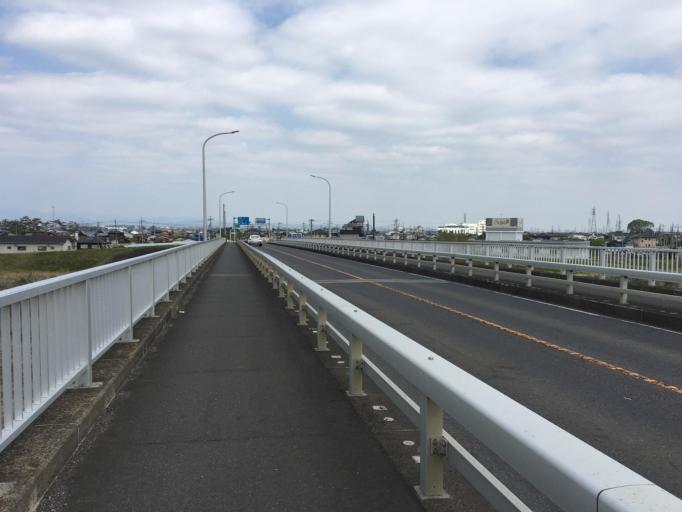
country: JP
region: Gunma
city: Isesaki
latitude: 36.2900
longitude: 139.1644
